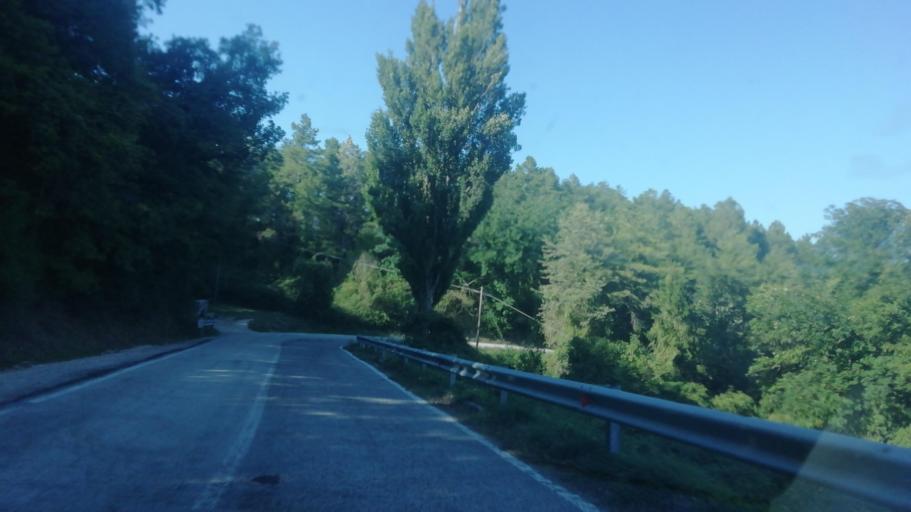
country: IT
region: The Marches
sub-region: Provincia di Pesaro e Urbino
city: Cagli
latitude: 43.5409
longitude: 12.6973
